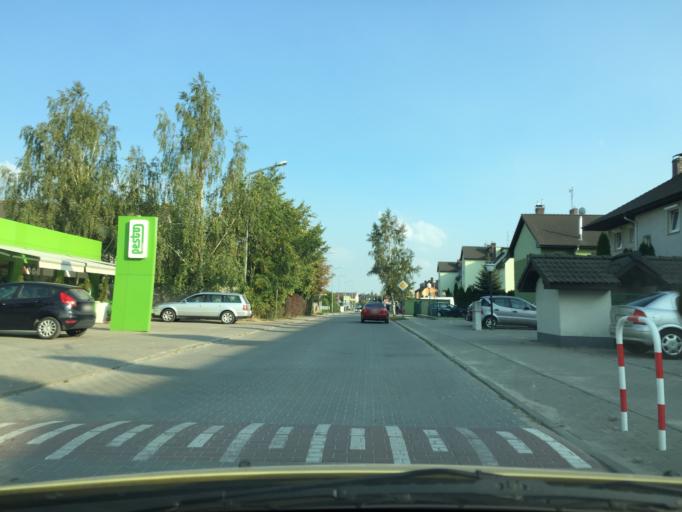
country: PL
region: Greater Poland Voivodeship
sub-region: Powiat poznanski
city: Plewiska
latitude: 52.3731
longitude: 16.8135
